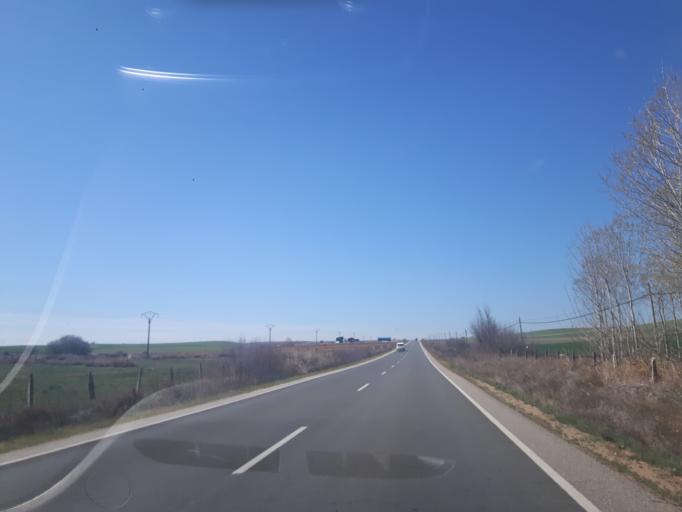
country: ES
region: Castille and Leon
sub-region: Provincia de Salamanca
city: Aldeaseca de Alba
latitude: 40.8453
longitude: -5.4620
